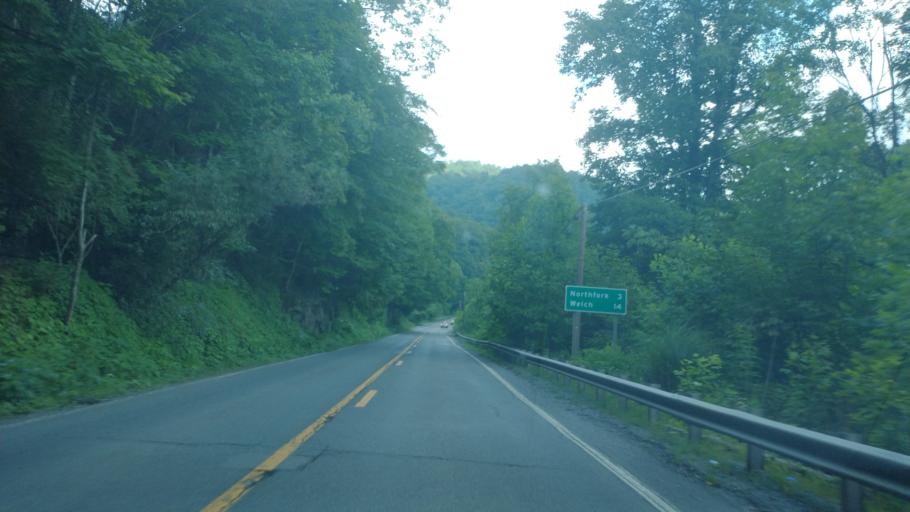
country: US
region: West Virginia
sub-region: Mercer County
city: Bluewell
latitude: 37.3853
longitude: -81.4164
